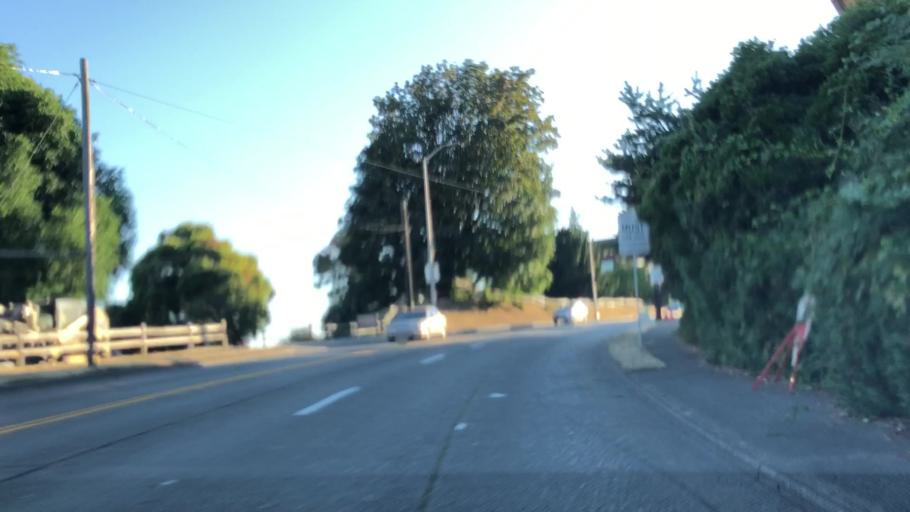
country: US
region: Washington
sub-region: King County
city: Seattle
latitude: 47.6326
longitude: -122.3899
